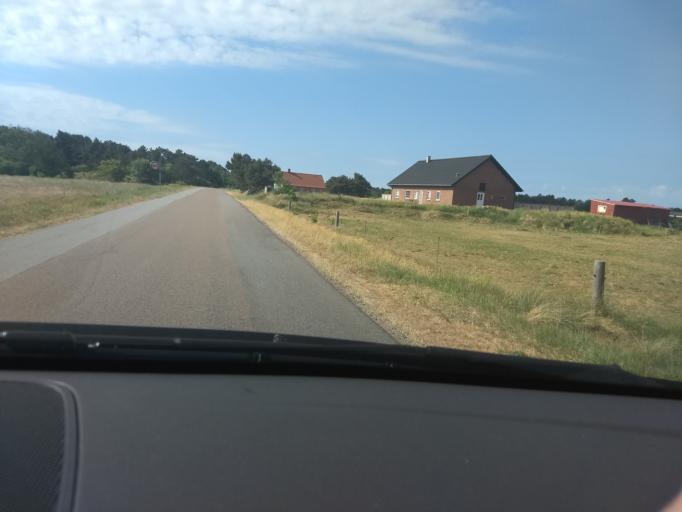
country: DE
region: Schleswig-Holstein
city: List
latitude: 55.0912
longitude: 8.5429
